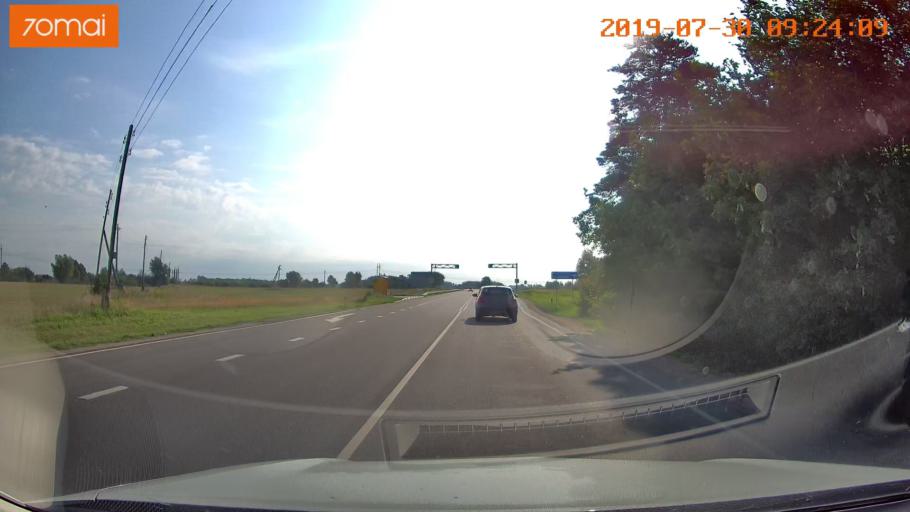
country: LT
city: Kybartai
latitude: 54.6333
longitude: 22.6886
